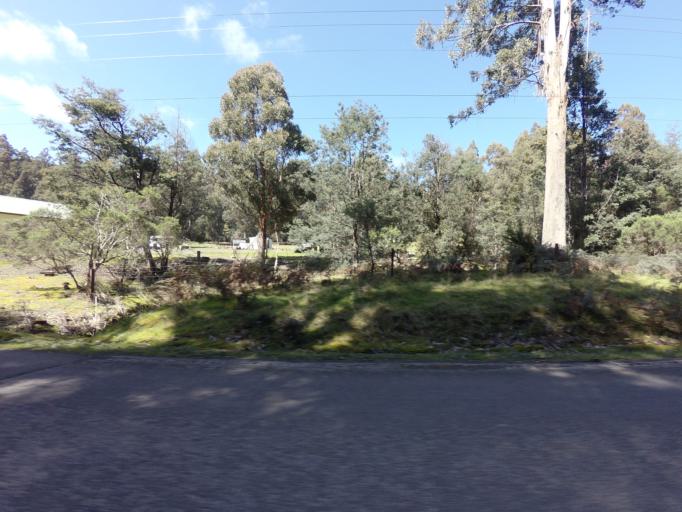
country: AU
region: Tasmania
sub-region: Derwent Valley
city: New Norfolk
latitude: -42.7585
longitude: 146.6164
